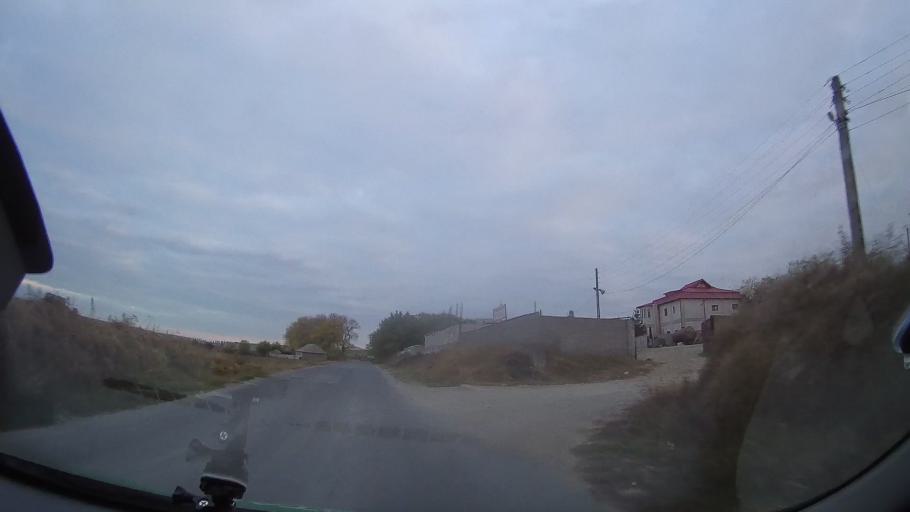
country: RO
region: Tulcea
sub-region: Comuna Mihai Bravu
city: Turda
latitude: 44.9687
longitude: 28.6290
